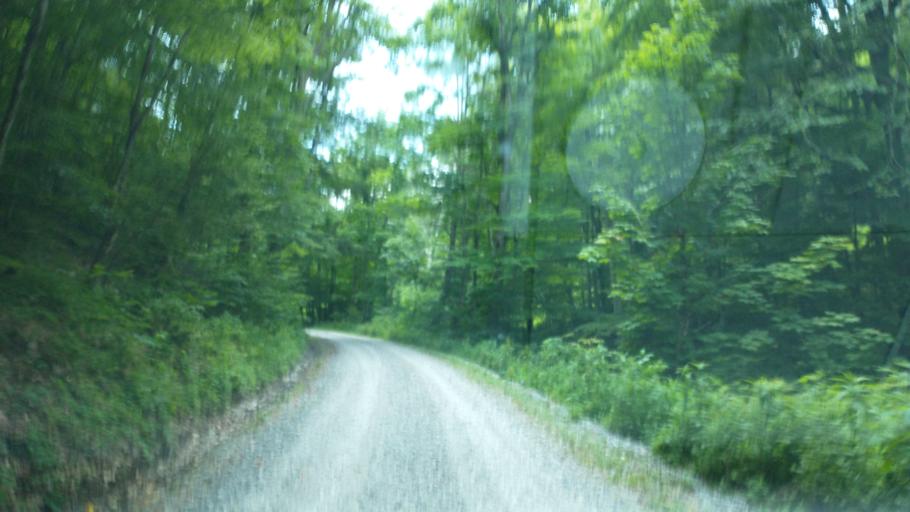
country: US
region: West Virginia
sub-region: Mercer County
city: Athens
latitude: 37.4281
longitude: -80.9968
